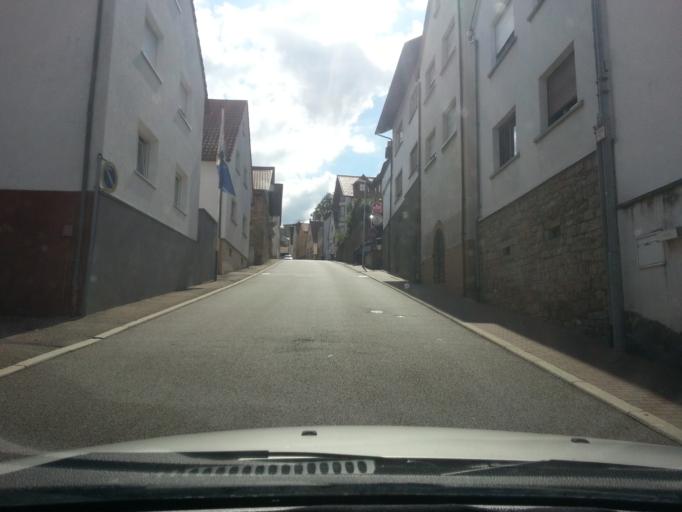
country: DE
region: Baden-Wuerttemberg
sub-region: Karlsruhe Region
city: Malsch
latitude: 49.2548
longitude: 8.6807
